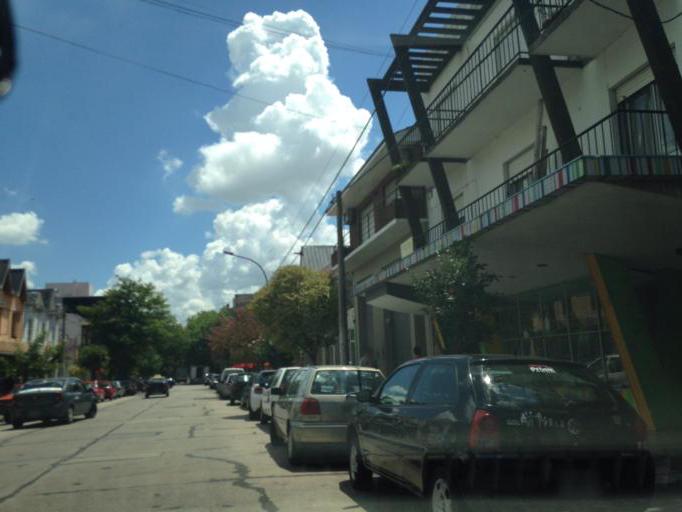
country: AR
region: Buenos Aires
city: Mar del Plata
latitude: -38.0171
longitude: -57.5431
